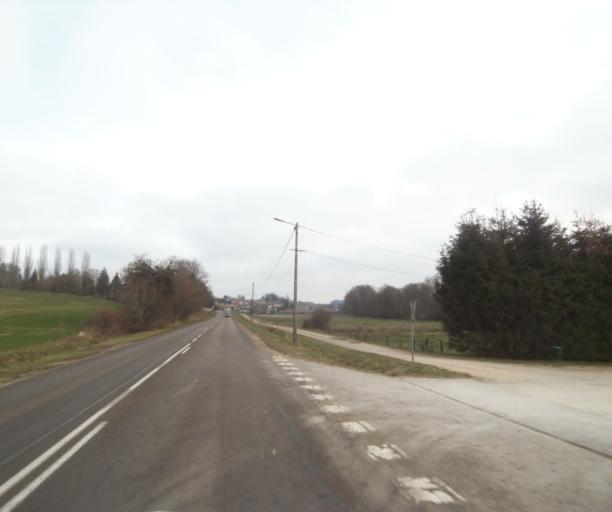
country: FR
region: Champagne-Ardenne
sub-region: Departement de la Haute-Marne
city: Chancenay
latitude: 48.6644
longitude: 4.9789
